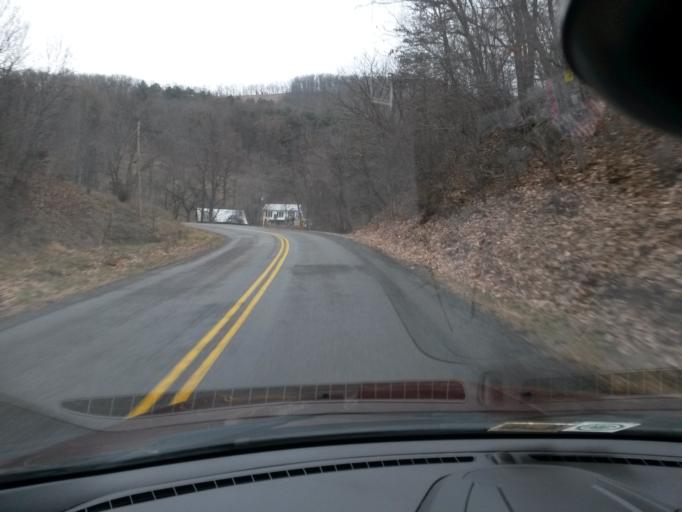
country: US
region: Virginia
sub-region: City of Lexington
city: Lexington
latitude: 37.8941
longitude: -79.5725
